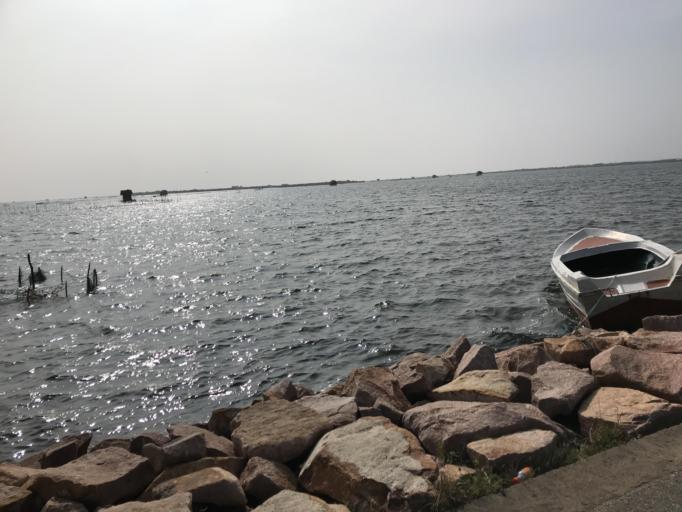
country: LK
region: Northern Province
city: Jaffna
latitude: 9.6541
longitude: 79.9993
